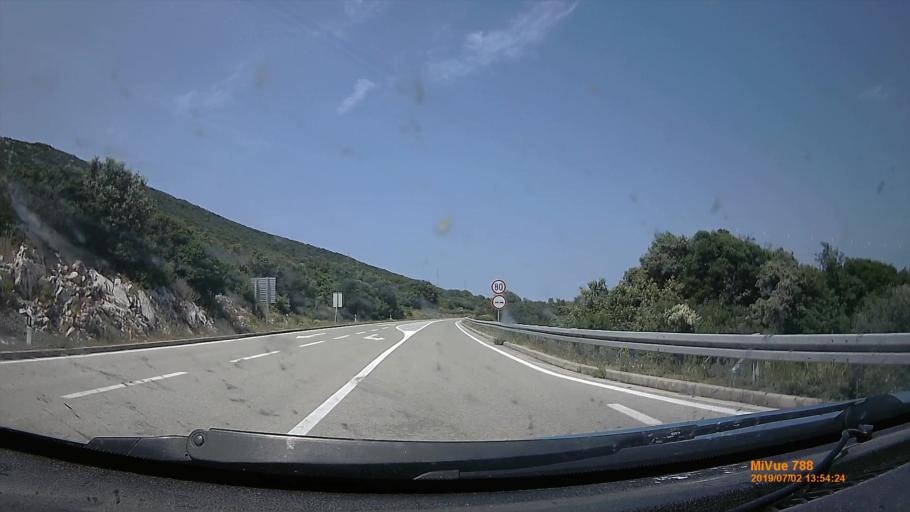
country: HR
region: Primorsko-Goranska
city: Mali Losinj
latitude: 44.6385
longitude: 14.3912
